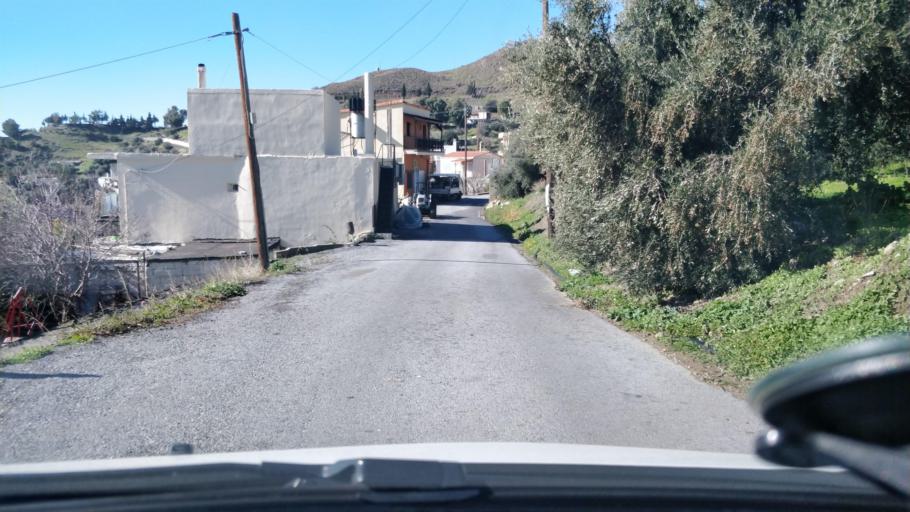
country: GR
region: Crete
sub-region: Nomos Irakleiou
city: Kastelli
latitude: 35.0420
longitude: 25.4481
